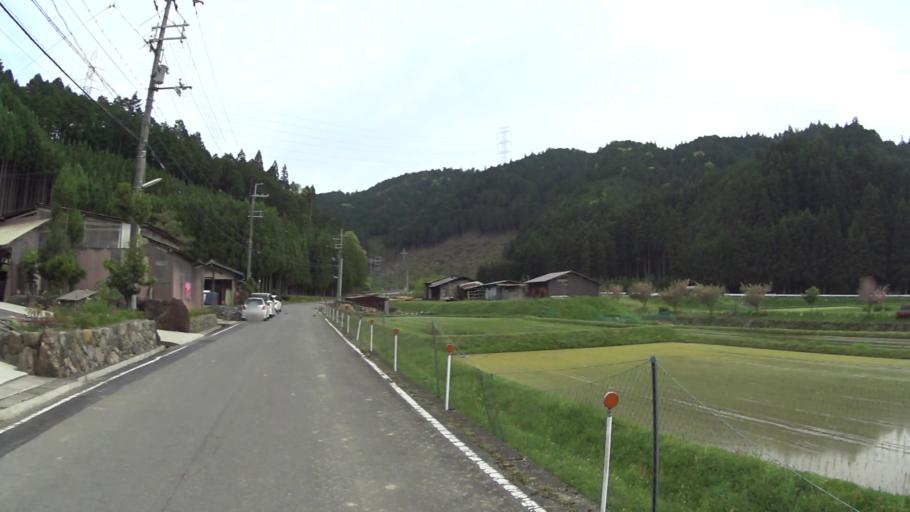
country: JP
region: Kyoto
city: Kameoka
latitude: 35.1267
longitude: 135.6285
